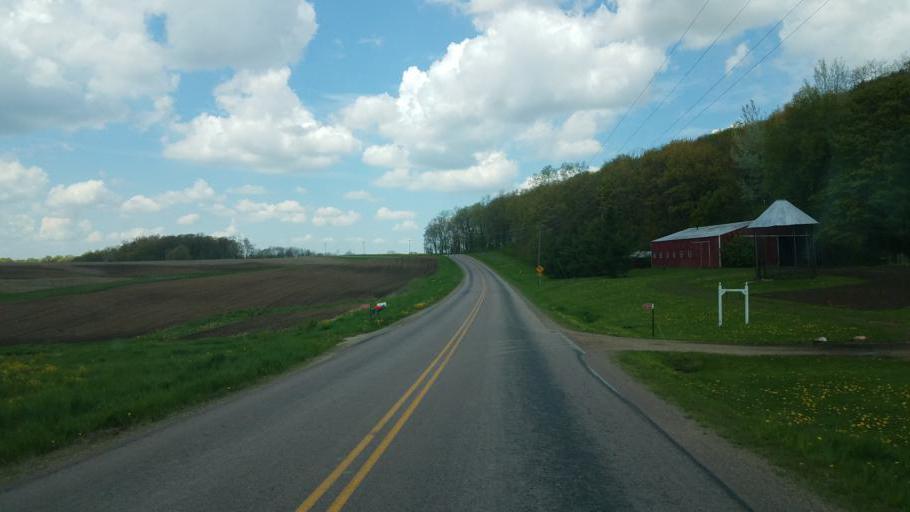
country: US
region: Wisconsin
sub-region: Vernon County
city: Hillsboro
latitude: 43.5888
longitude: -90.3740
